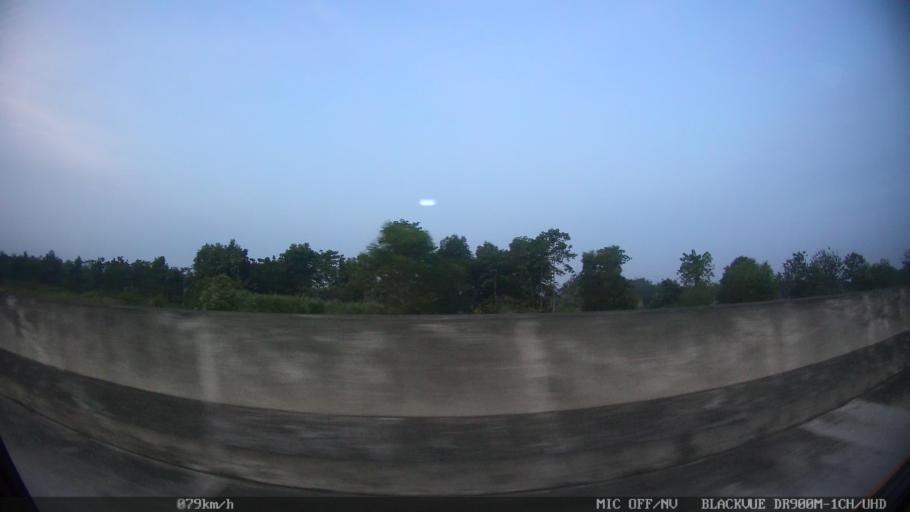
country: ID
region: Lampung
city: Kalianda
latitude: -5.6808
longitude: 105.6098
